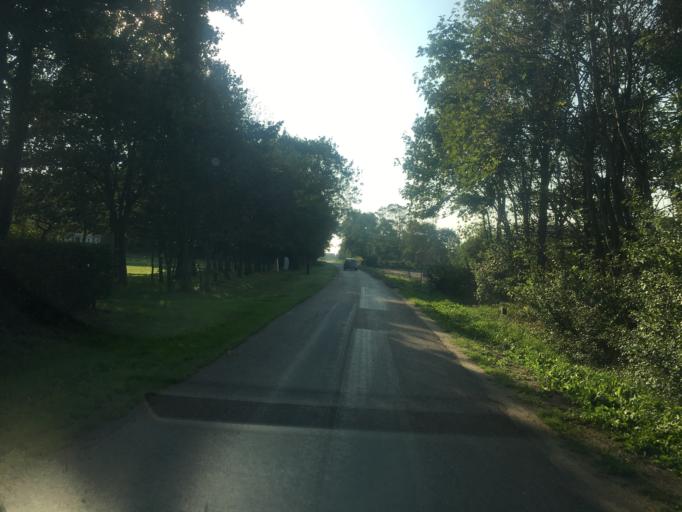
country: DE
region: Schleswig-Holstein
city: Bramstedtlund
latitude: 54.9209
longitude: 9.0478
